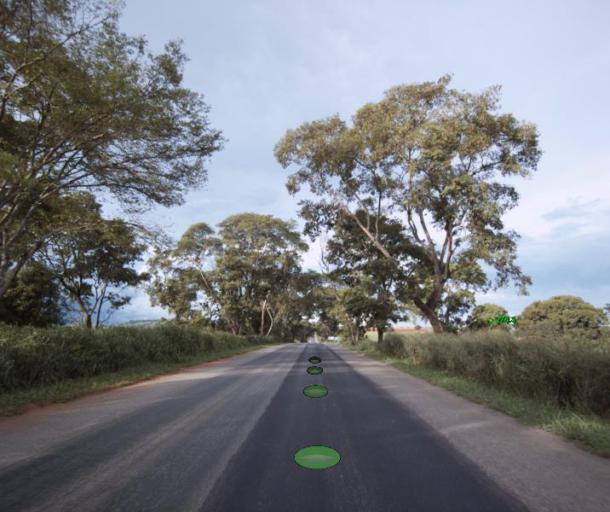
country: BR
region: Goias
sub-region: Itapaci
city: Itapaci
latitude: -15.1173
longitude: -49.4962
